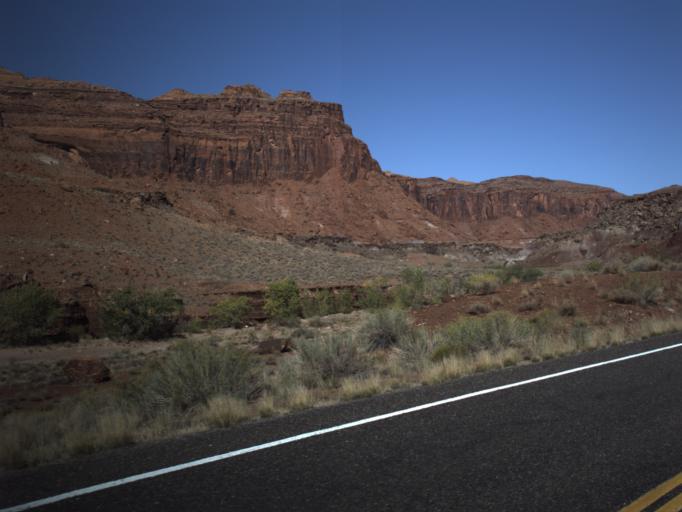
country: US
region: Utah
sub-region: San Juan County
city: Blanding
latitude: 37.9010
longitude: -110.4498
